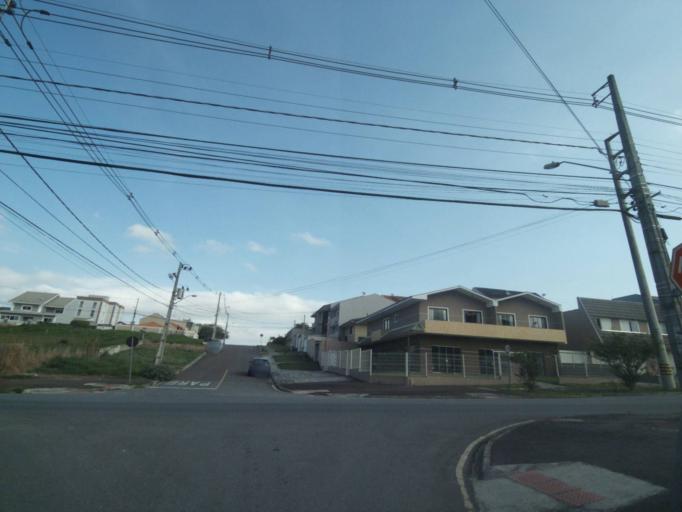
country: BR
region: Parana
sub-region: Pinhais
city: Pinhais
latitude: -25.4092
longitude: -49.2143
